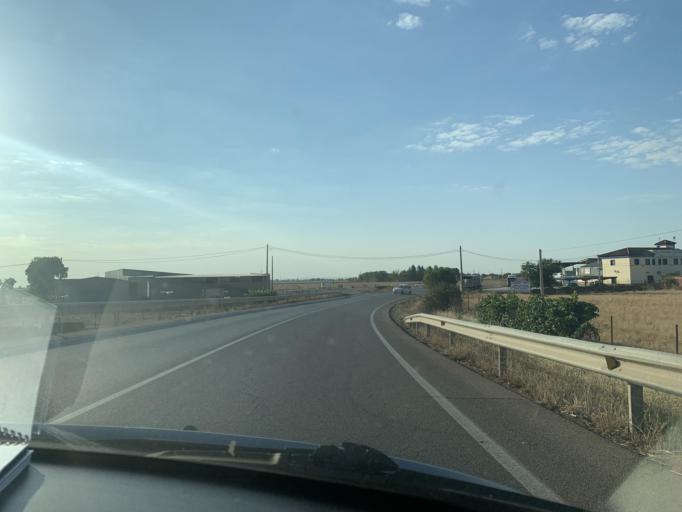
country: ES
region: Castille-La Mancha
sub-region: Provincia de Ciudad Real
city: Argamasilla de Alba
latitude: 39.1705
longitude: -3.2310
